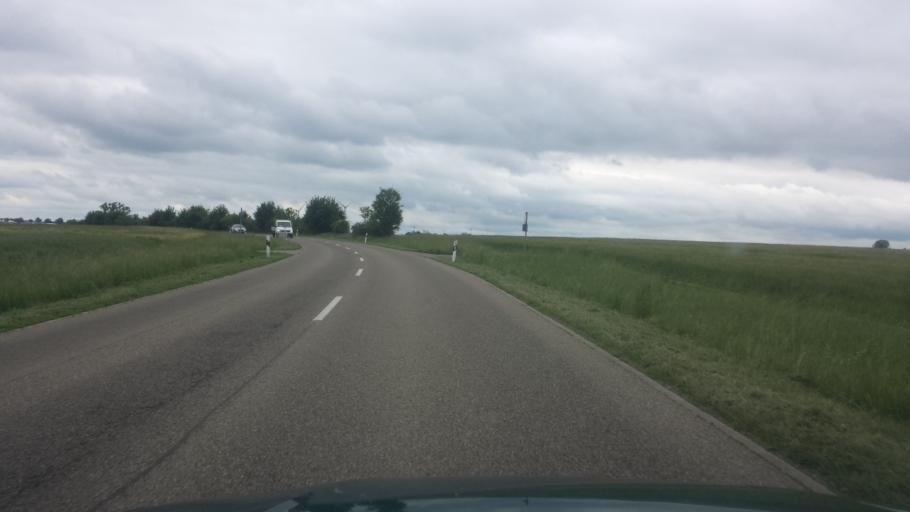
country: DE
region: Baden-Wuerttemberg
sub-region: Regierungsbezirk Stuttgart
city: Rot am See
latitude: 49.2261
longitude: 10.0136
